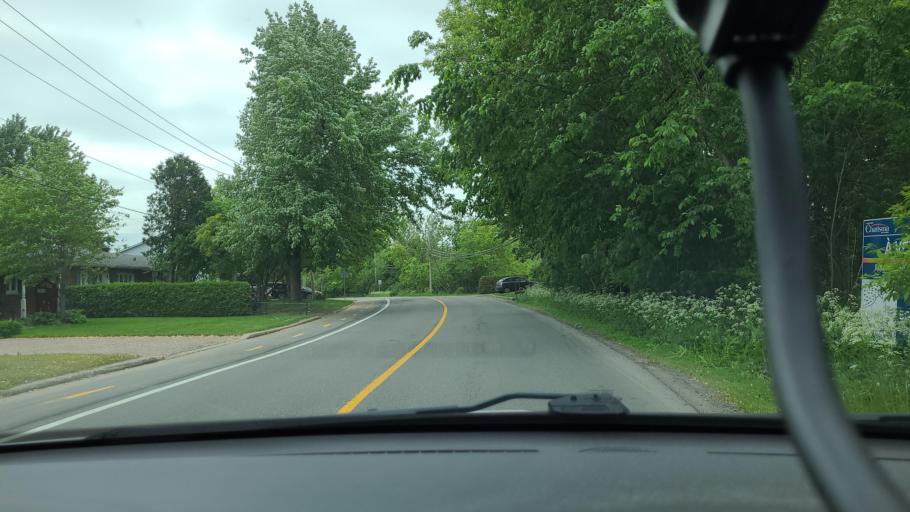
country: CA
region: Quebec
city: Bois-des-Filion
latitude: 45.6398
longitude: -73.7601
